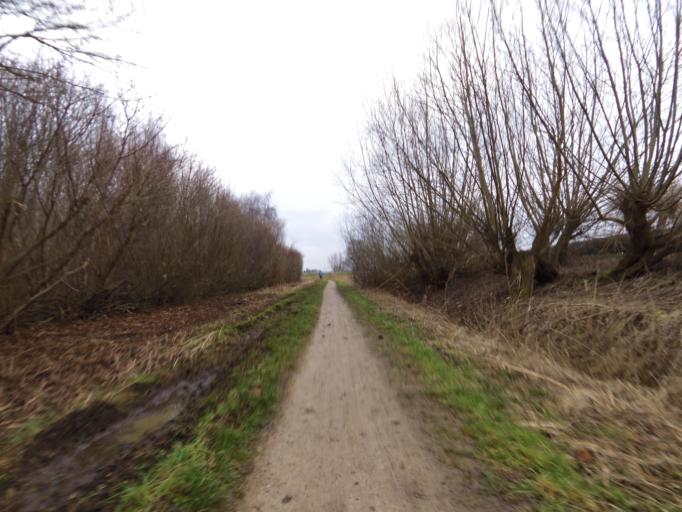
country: GB
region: England
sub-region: Cambridgeshire
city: Waterbeach
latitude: 52.2597
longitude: 0.1987
